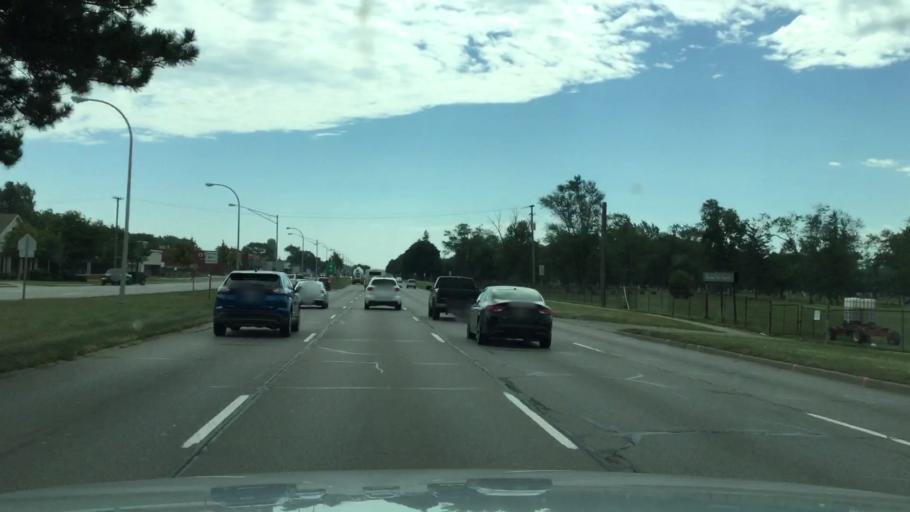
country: US
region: Michigan
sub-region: Oakland County
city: Berkley
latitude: 42.5096
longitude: -83.1784
